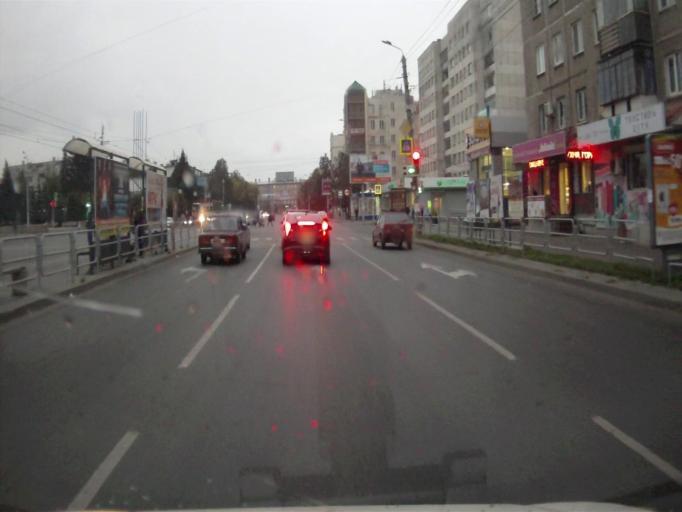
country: RU
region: Chelyabinsk
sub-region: Gorod Chelyabinsk
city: Chelyabinsk
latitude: 55.1790
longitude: 61.3996
